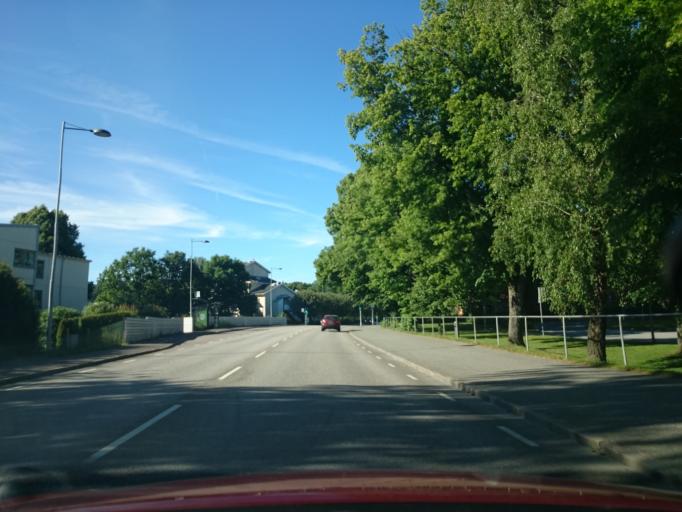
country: SE
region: Vaestra Goetaland
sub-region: Lerums Kommun
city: Lerum
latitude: 57.7726
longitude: 12.2740
